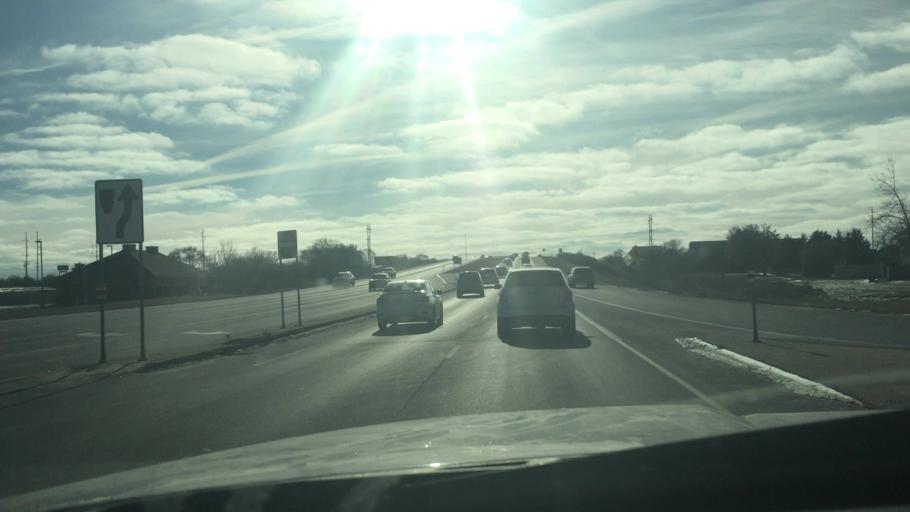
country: US
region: Minnesota
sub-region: Stearns County
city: Waite Park
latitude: 45.5659
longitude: -94.2060
